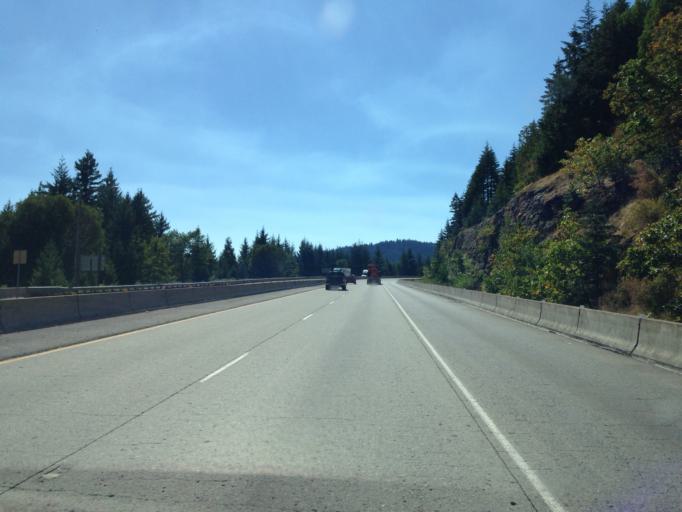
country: US
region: Oregon
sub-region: Jackson County
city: Ashland
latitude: 42.0851
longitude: -122.6011
